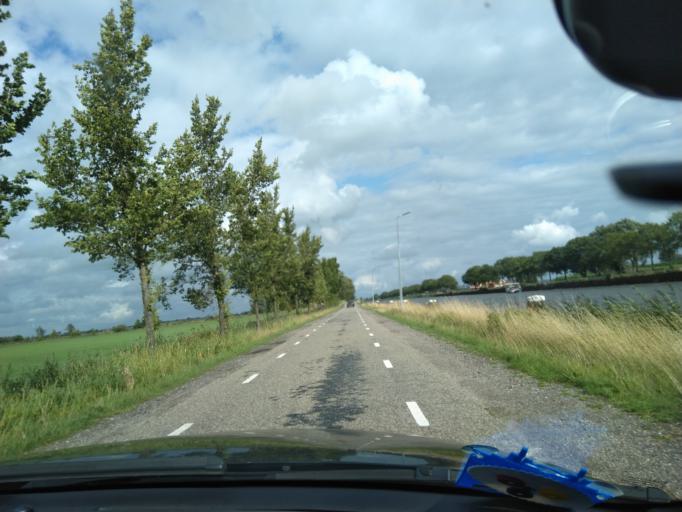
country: NL
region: Groningen
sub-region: Gemeente Zuidhorn
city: Grijpskerk
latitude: 53.2504
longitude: 6.3227
